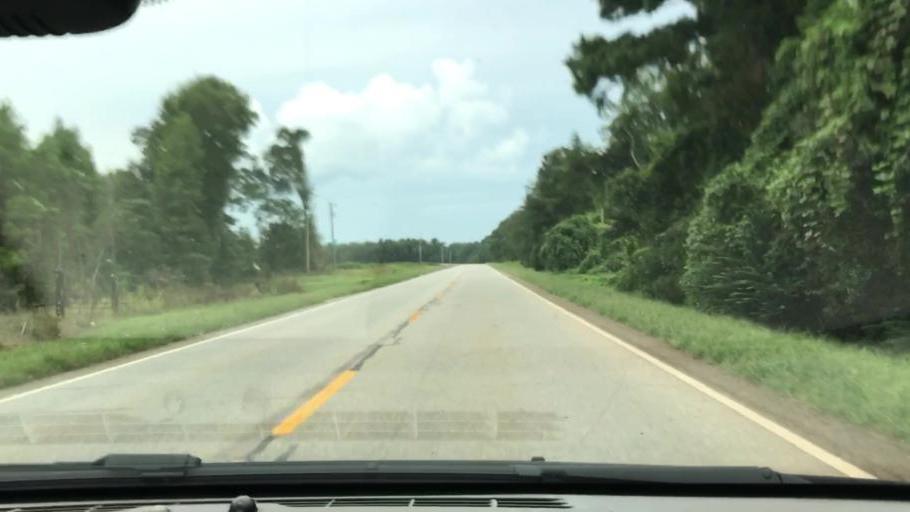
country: US
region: Georgia
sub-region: Early County
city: Blakely
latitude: 31.3165
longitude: -85.0370
